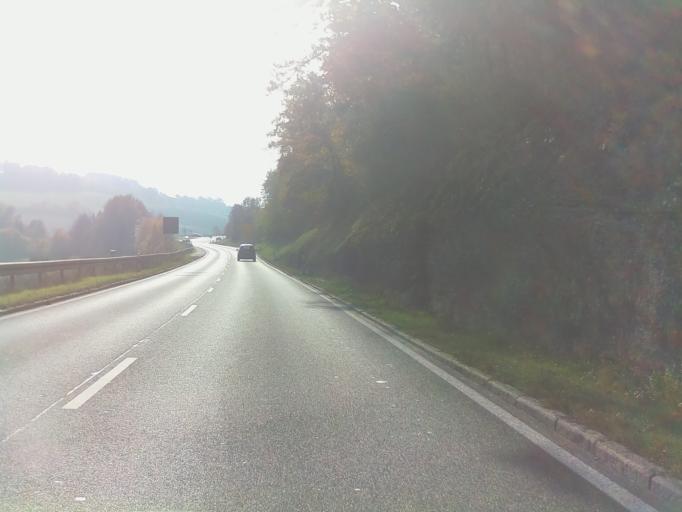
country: DE
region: Baden-Wuerttemberg
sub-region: Regierungsbezirk Stuttgart
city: Bad Mergentheim
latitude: 49.4574
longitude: 9.7647
